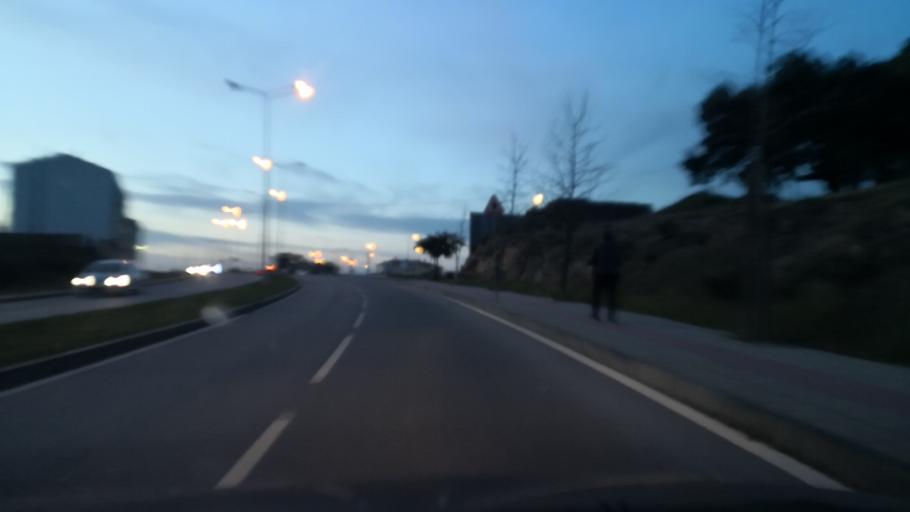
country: PT
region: Castelo Branco
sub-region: Castelo Branco
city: Castelo Branco
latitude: 39.8323
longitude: -7.4874
